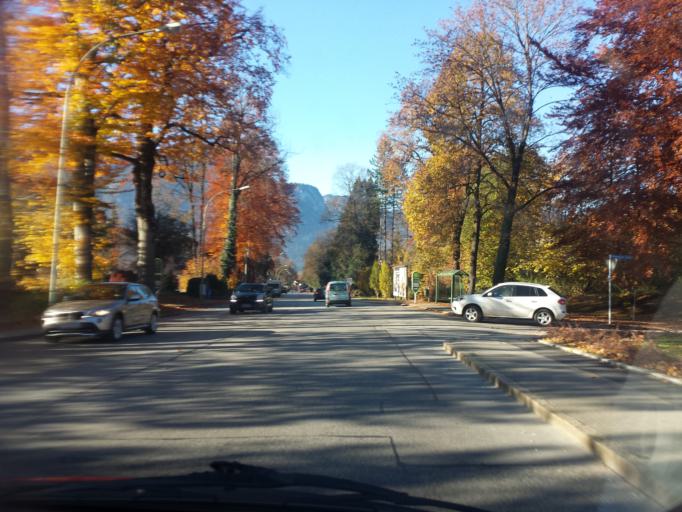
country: DE
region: Bavaria
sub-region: Upper Bavaria
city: Garmisch-Partenkirchen
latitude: 47.4865
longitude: 11.1176
